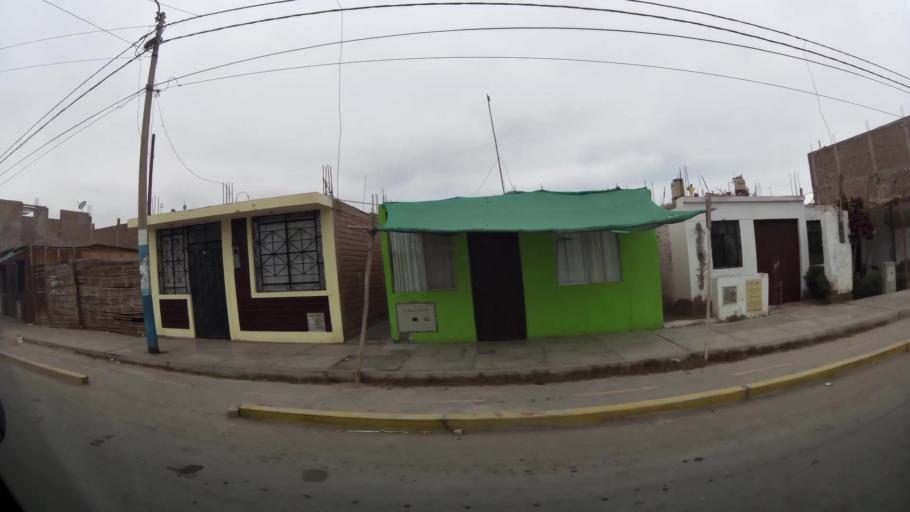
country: PE
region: Ica
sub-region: Provincia de Pisco
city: Pisco
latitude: -13.7229
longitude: -76.2049
